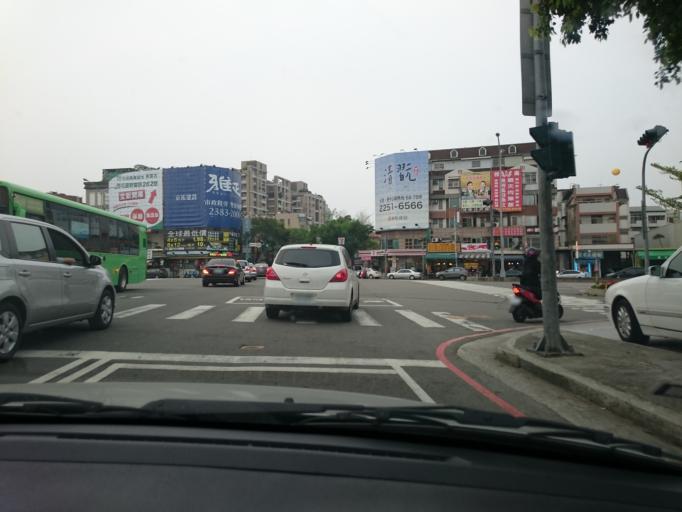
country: TW
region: Taiwan
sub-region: Taichung City
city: Taichung
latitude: 24.1611
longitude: 120.6339
